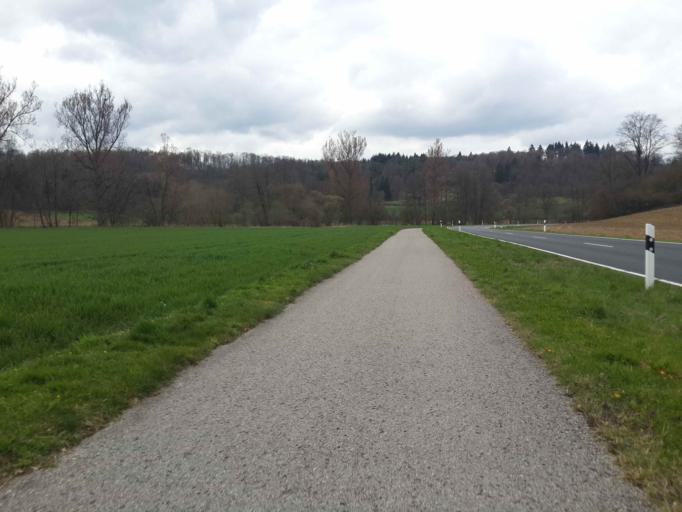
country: DE
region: Baden-Wuerttemberg
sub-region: Karlsruhe Region
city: Adelsheim
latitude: 49.3870
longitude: 9.3913
